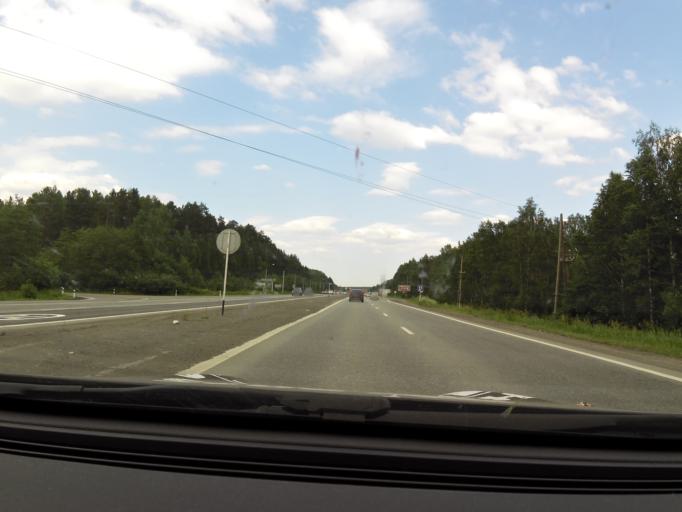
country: RU
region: Sverdlovsk
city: Severka
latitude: 56.8411
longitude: 60.1918
